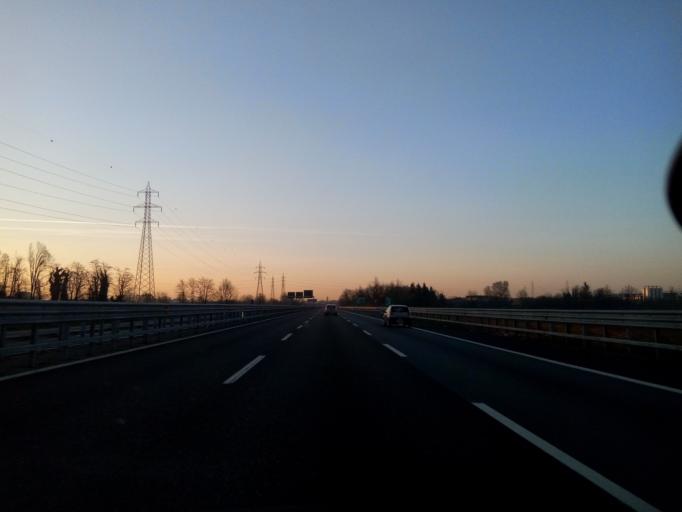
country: IT
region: Lombardy
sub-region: Citta metropolitana di Milano
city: Figino
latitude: 45.4829
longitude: 9.0711
